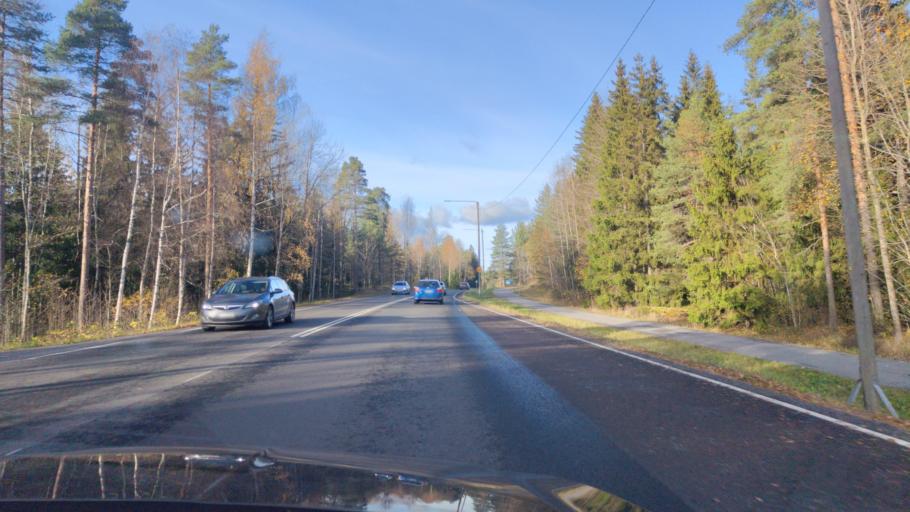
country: FI
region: Varsinais-Suomi
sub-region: Turku
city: Kaarina
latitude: 60.4555
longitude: 22.3676
